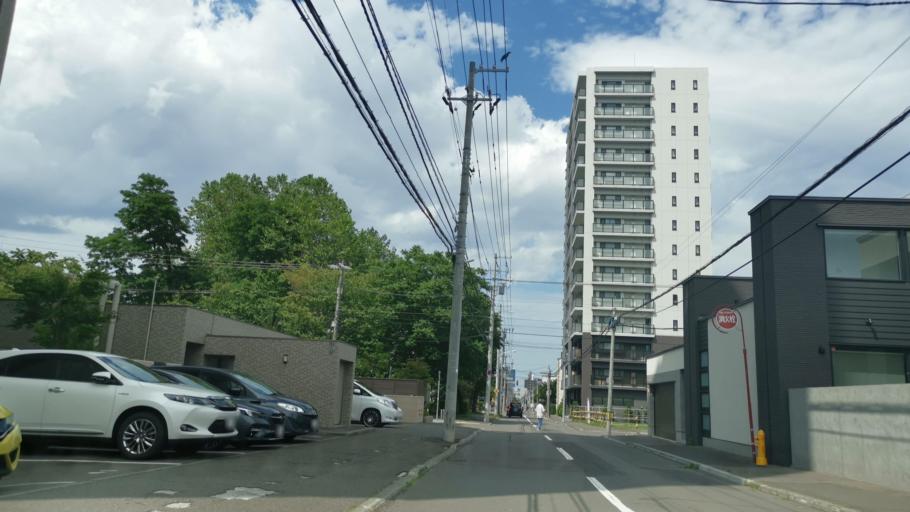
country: JP
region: Hokkaido
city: Sapporo
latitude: 43.0398
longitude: 141.3452
